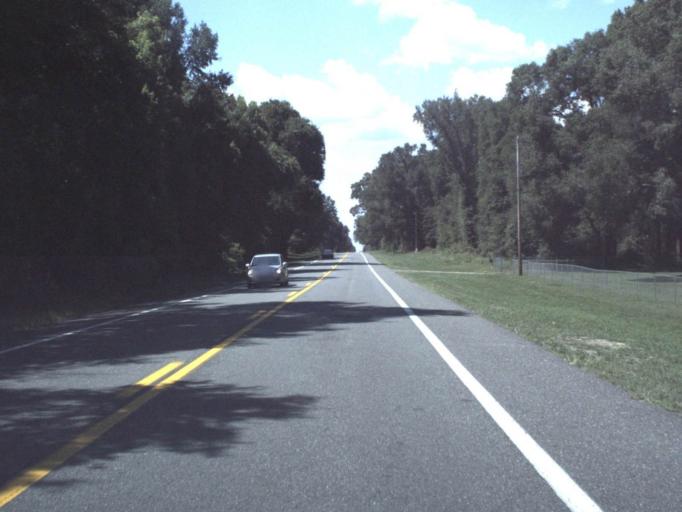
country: US
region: Florida
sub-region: Alachua County
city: High Springs
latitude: 29.9781
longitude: -82.7099
